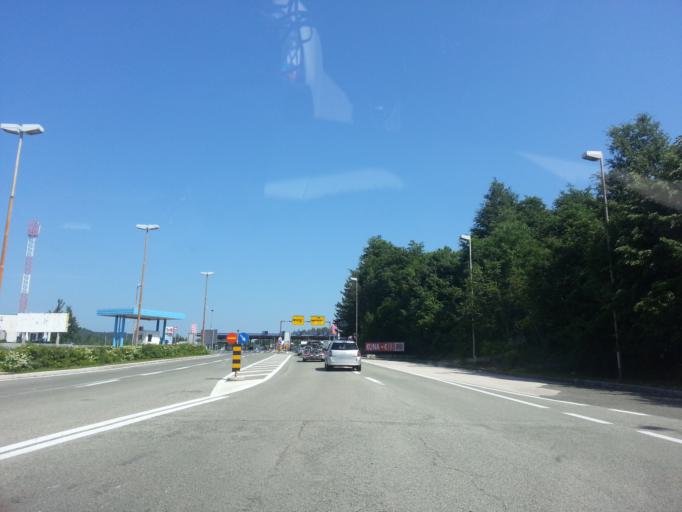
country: SI
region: Ilirska Bistrica
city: Ilirska Bistrica
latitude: 45.4887
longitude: 14.2786
